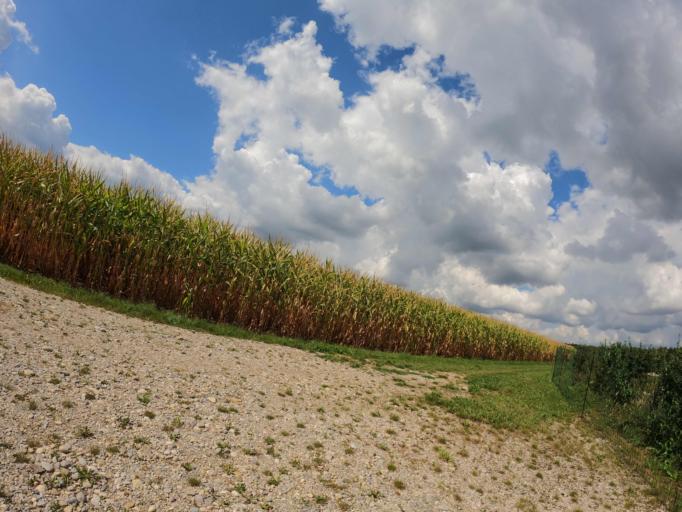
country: DE
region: Bavaria
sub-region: Upper Bavaria
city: Brunnthal
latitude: 48.0080
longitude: 11.6766
